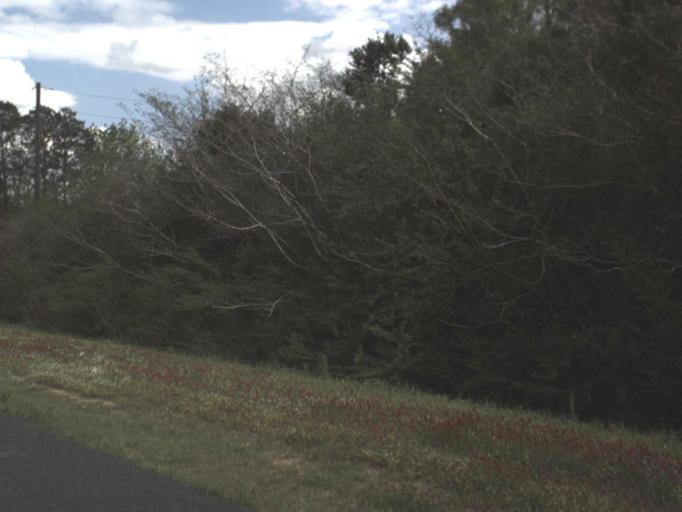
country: US
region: Florida
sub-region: Okaloosa County
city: Crestview
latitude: 30.8076
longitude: -86.5495
